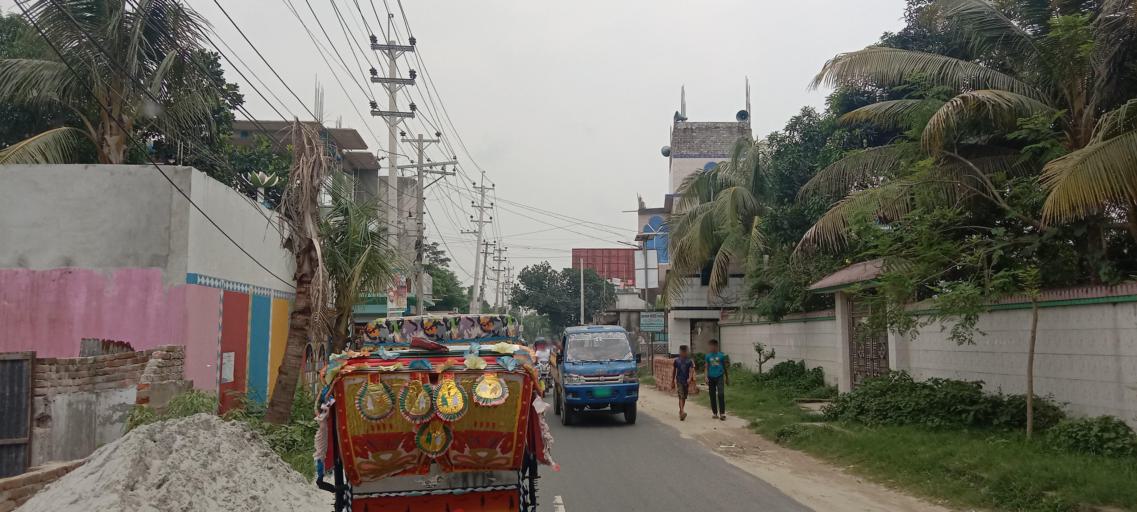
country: BD
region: Dhaka
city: Azimpur
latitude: 23.7094
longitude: 90.3470
